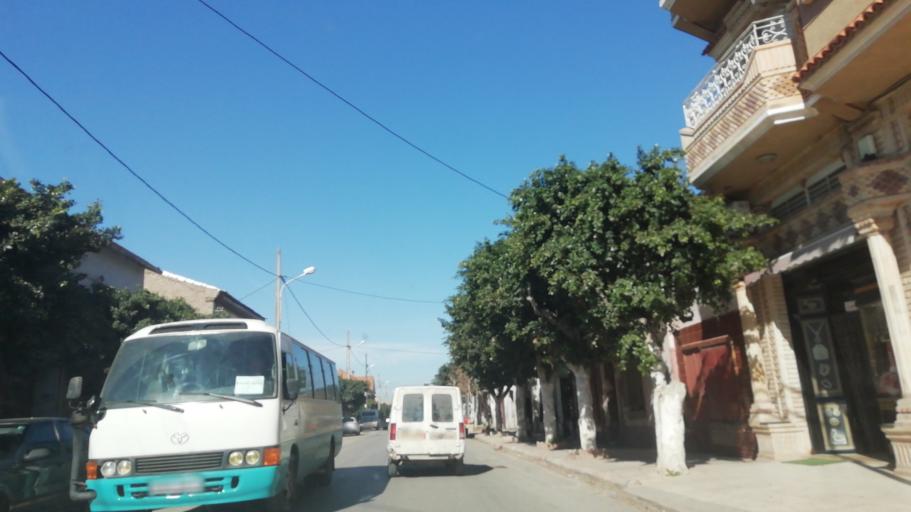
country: DZ
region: Oran
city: Es Senia
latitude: 35.6115
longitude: -0.5784
